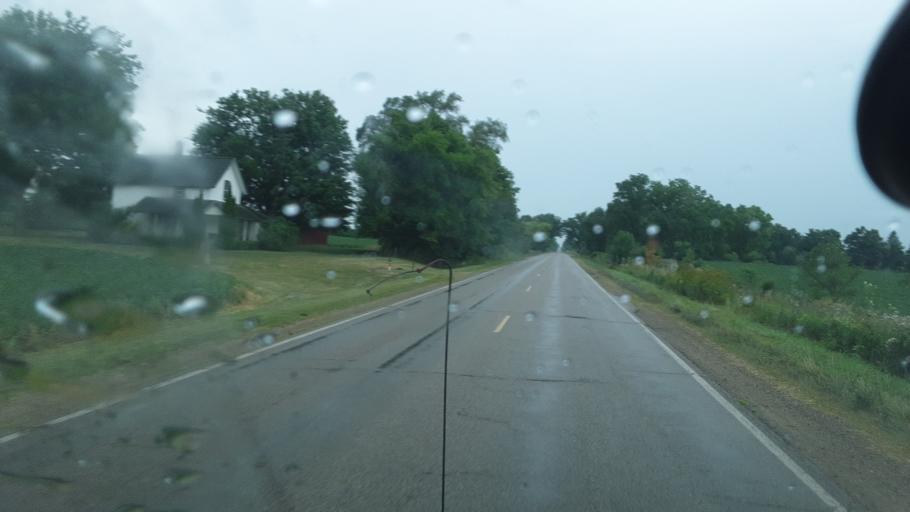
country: US
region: Michigan
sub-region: Hillsdale County
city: Reading
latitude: 41.7081
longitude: -84.7530
